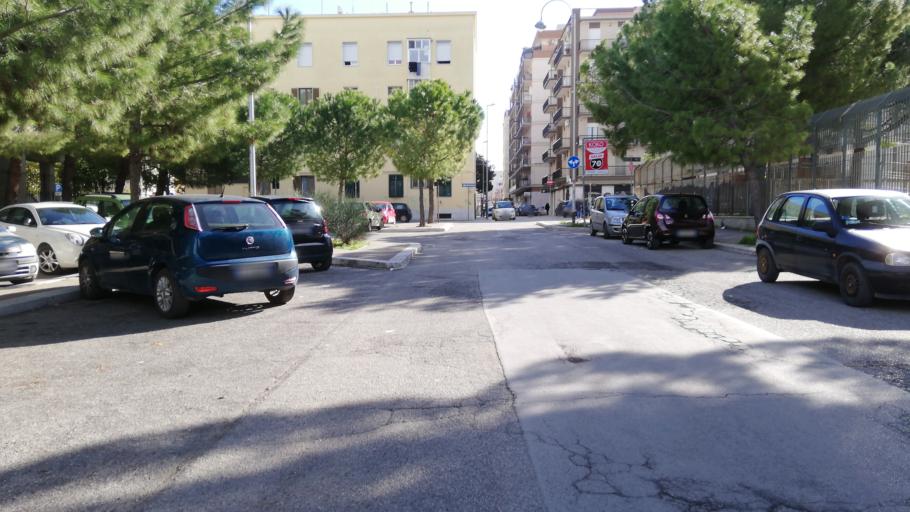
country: IT
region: Apulia
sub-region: Provincia di Barletta - Andria - Trani
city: Andria
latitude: 41.2327
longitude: 16.3028
